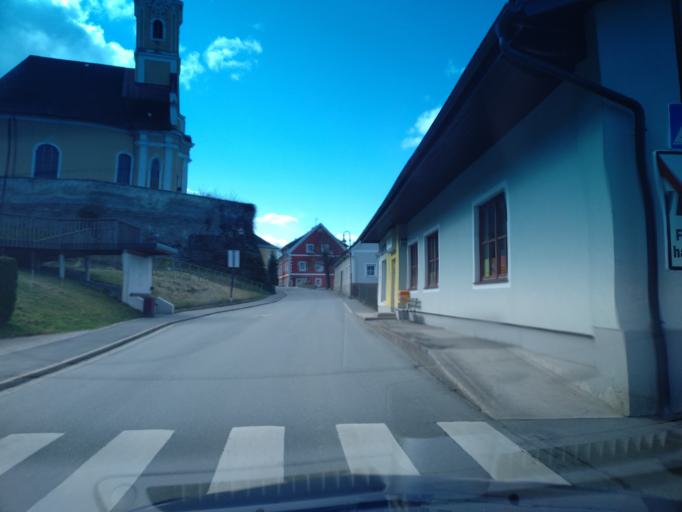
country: AT
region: Styria
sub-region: Politischer Bezirk Leibnitz
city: Sankt Johann im Saggautal
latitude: 46.7032
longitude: 15.4008
